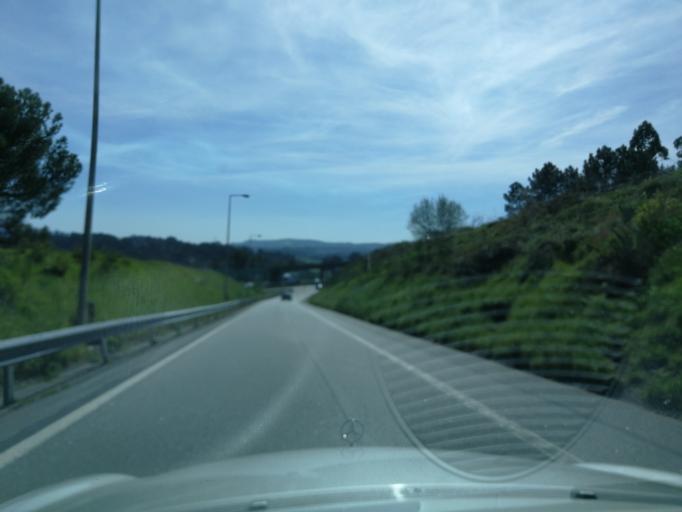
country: PT
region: Braga
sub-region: Vila Nova de Famalicao
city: Vila Nova de Famalicao
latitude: 41.3747
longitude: -8.5033
